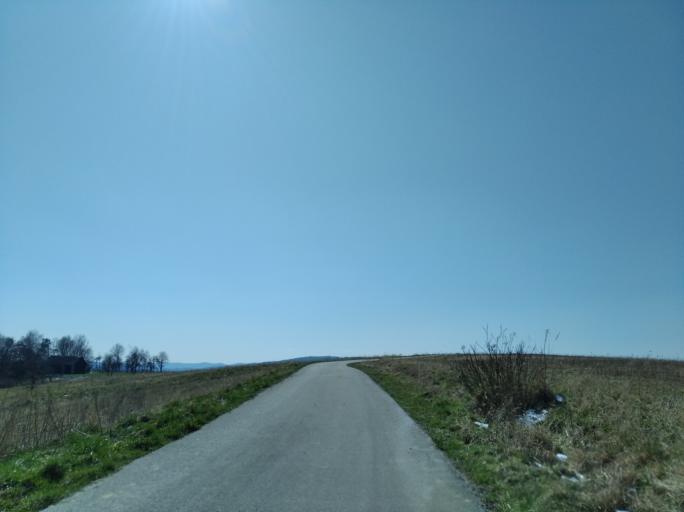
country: PL
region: Subcarpathian Voivodeship
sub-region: Powiat strzyzowski
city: Strzyzow
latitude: 49.8554
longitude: 21.8151
